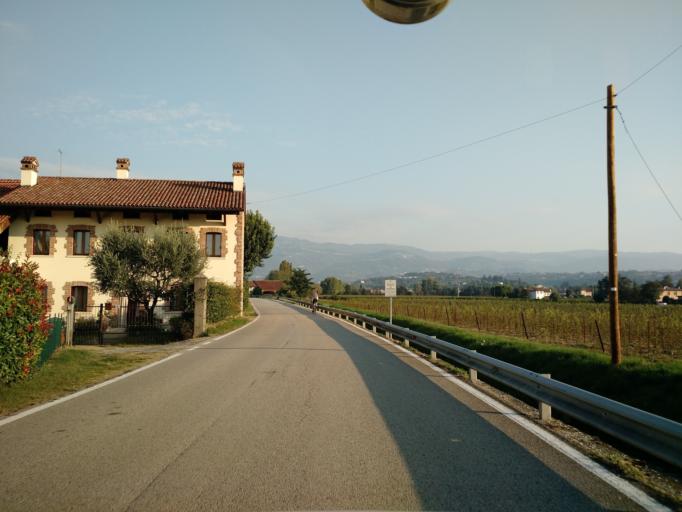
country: IT
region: Veneto
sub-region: Provincia di Vicenza
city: Sarcedo
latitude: 45.6952
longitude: 11.5393
